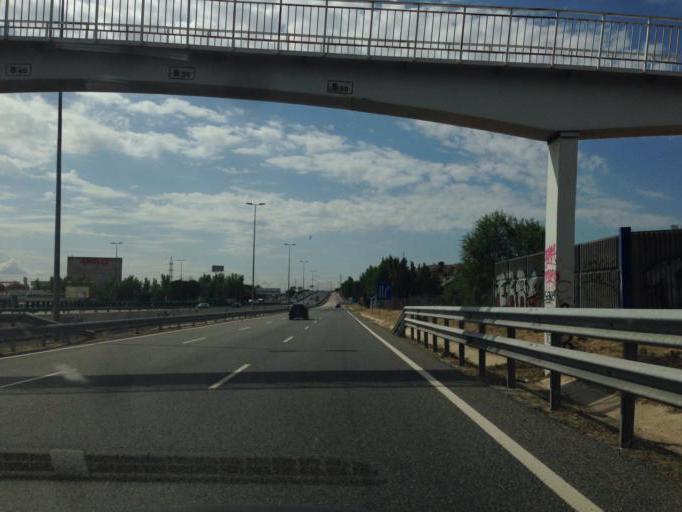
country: ES
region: Madrid
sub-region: Provincia de Madrid
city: San Sebastian de los Reyes
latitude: 40.5888
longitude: -3.5836
